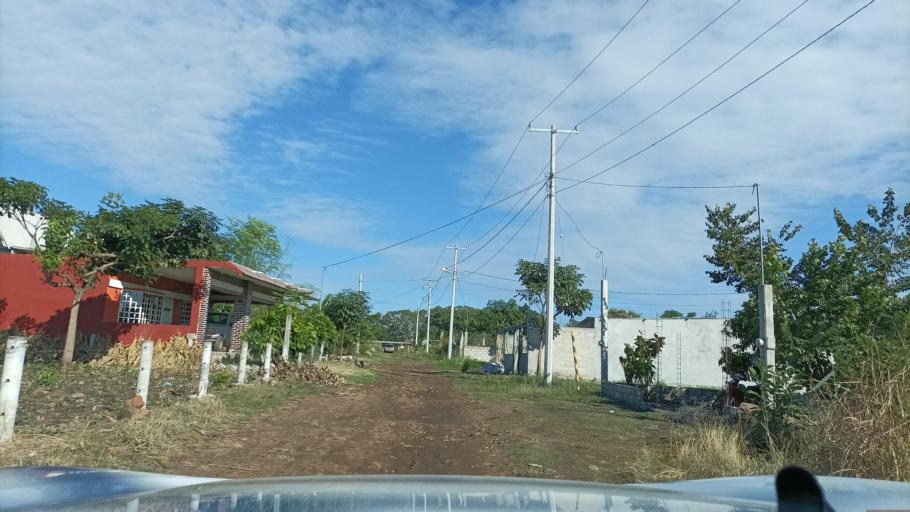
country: MX
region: Veracruz
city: Paso del Macho
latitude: 18.9725
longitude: -96.7130
